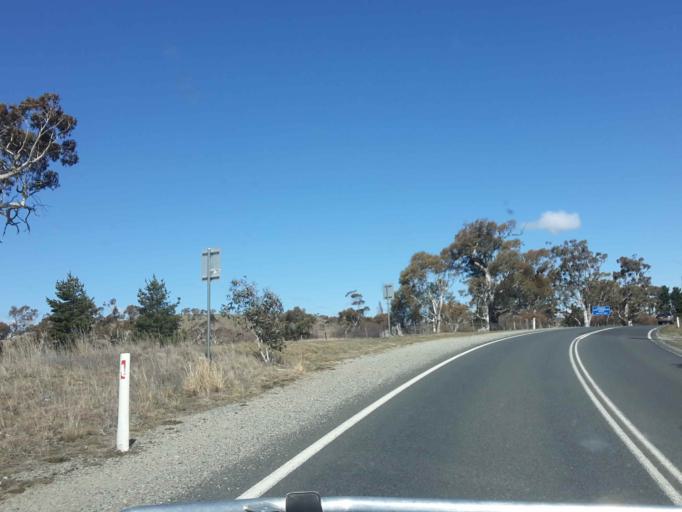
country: AU
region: New South Wales
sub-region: Snowy River
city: Jindabyne
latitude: -36.4299
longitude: 148.6100
